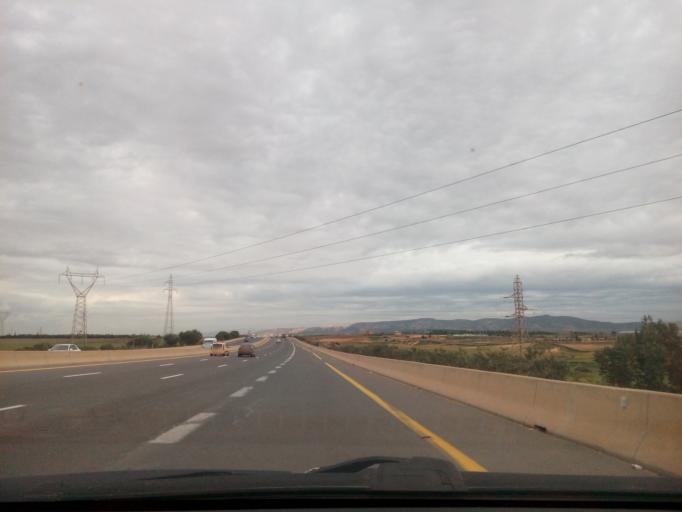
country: DZ
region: Mascara
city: Sig
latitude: 35.5431
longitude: -0.3754
